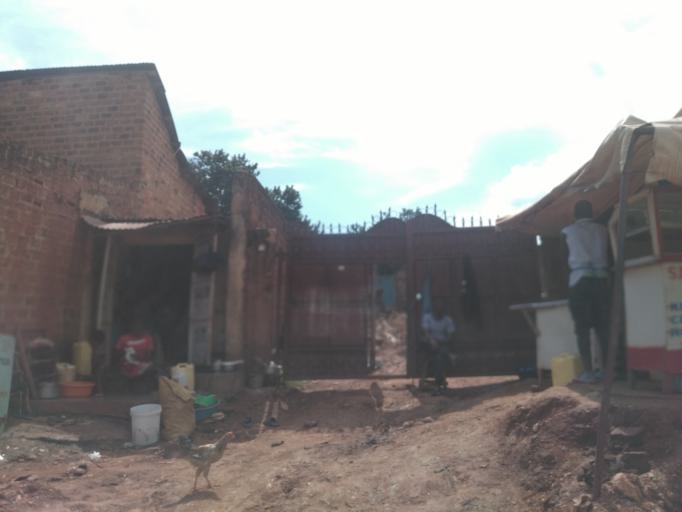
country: UG
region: Central Region
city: Kampala Central Division
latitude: 0.3437
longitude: 32.5667
